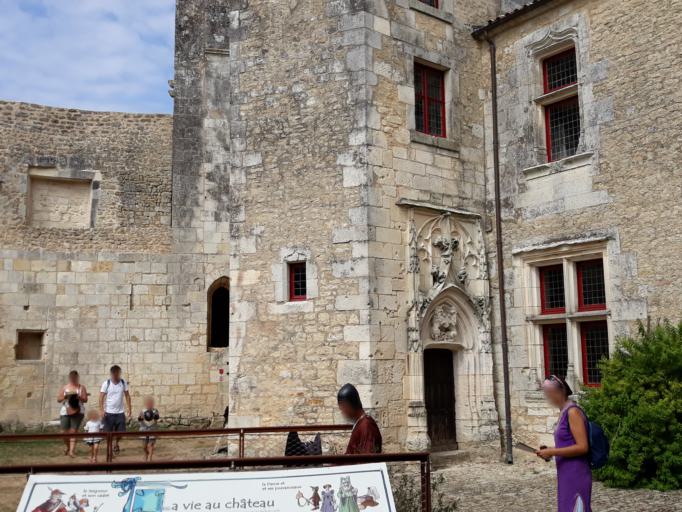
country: FR
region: Poitou-Charentes
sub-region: Departement de la Charente-Maritime
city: Saint-Agnant
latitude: 45.8206
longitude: -0.9510
